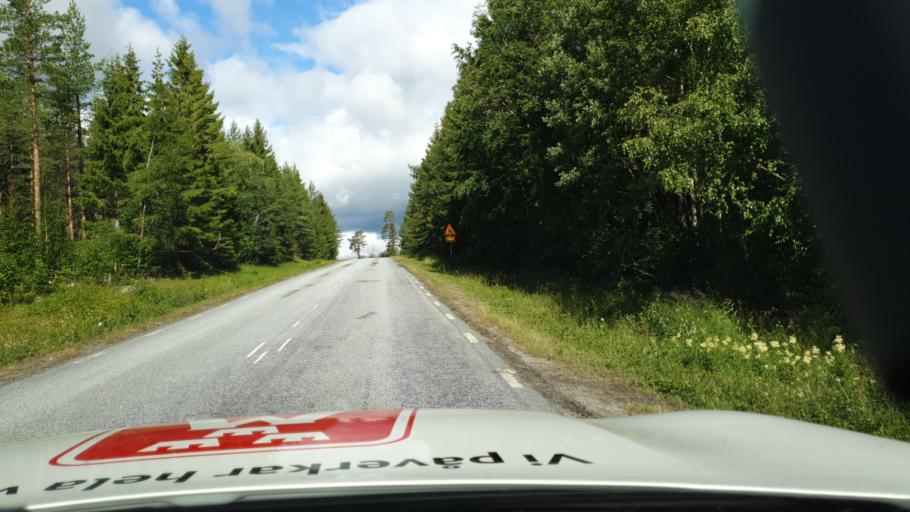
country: SE
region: Vaesterbotten
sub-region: Umea Kommun
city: Roback
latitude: 63.6744
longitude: 20.1107
